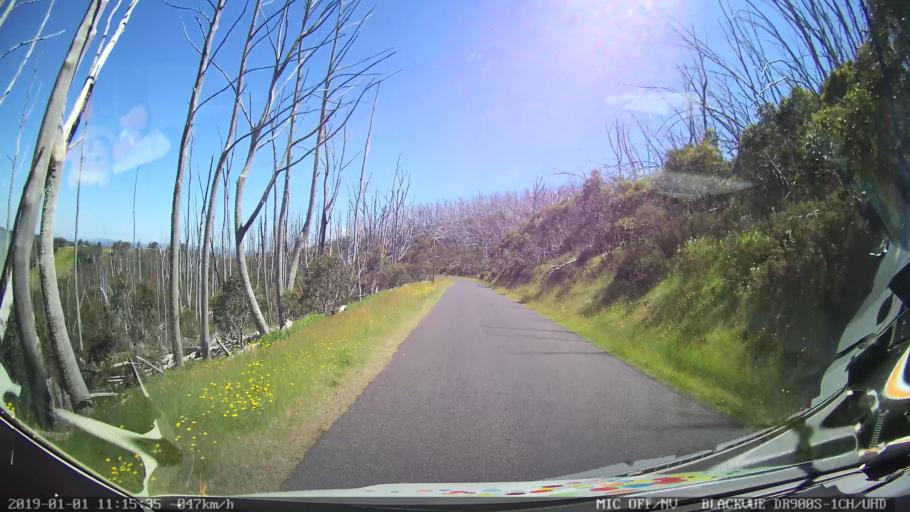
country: AU
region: New South Wales
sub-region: Snowy River
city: Jindabyne
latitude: -35.9441
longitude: 148.3873
